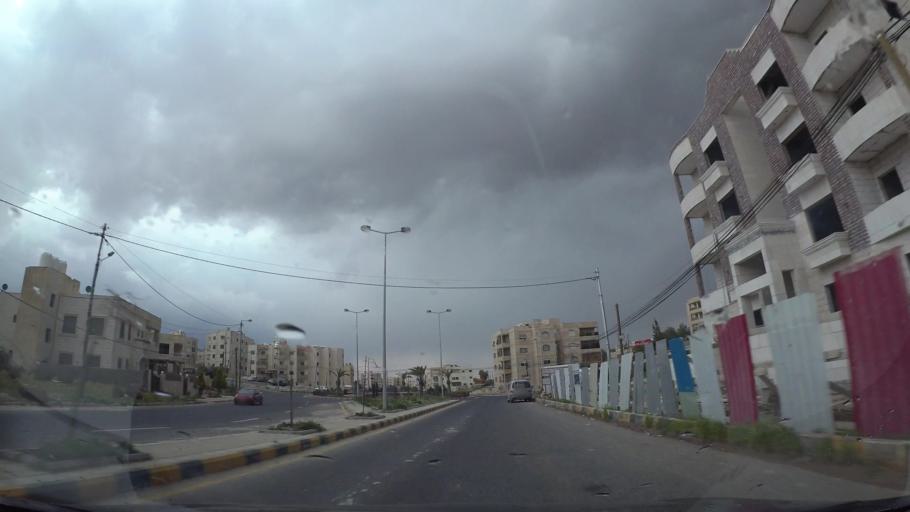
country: JO
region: Amman
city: Amman
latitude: 32.0094
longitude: 35.9606
